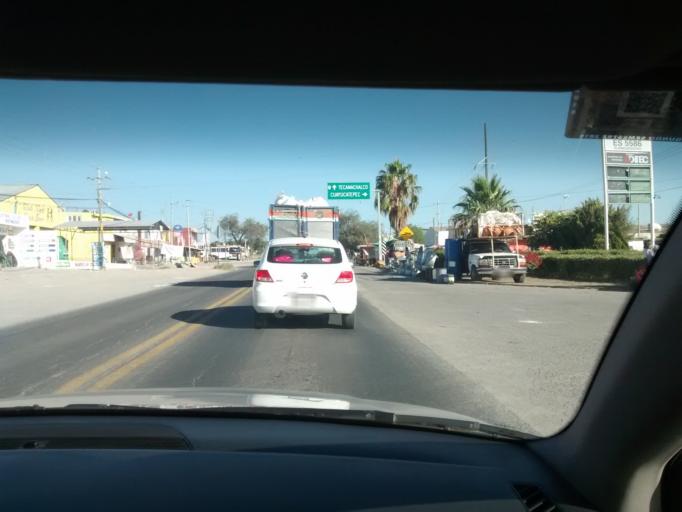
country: MX
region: Puebla
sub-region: Tehuacan
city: Magdalena Cuayucatepec
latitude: 18.5185
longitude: -97.5034
